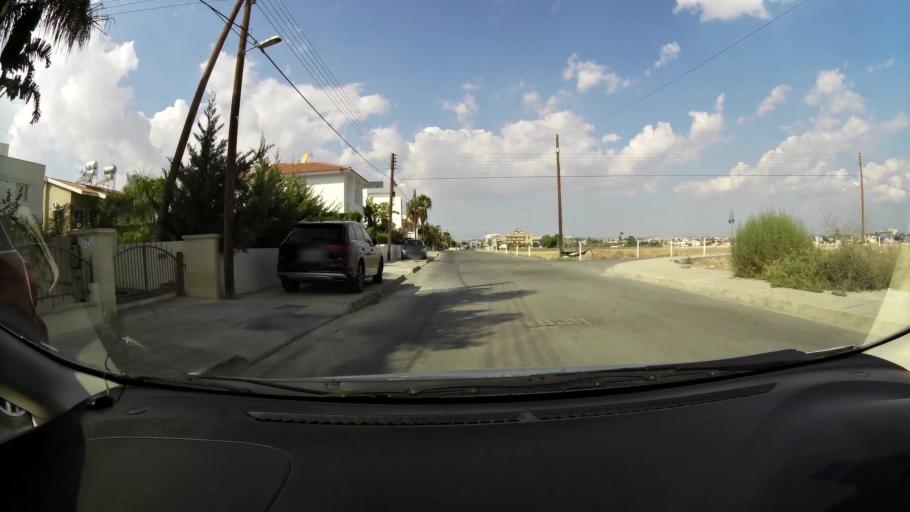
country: CY
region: Larnaka
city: Dhromolaxia
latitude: 34.9082
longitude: 33.5872
